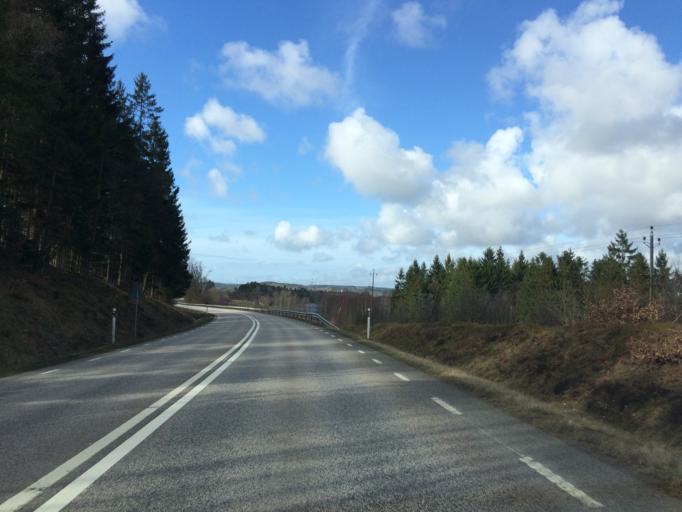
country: SE
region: Halland
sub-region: Laholms Kommun
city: Knared
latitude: 56.5012
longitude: 13.3628
